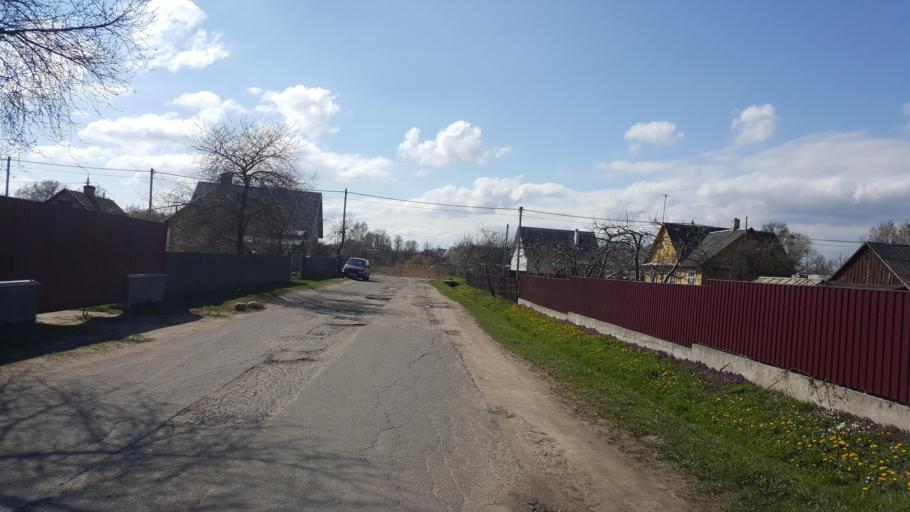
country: BY
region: Brest
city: Kamyanyets
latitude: 52.4019
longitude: 23.8140
